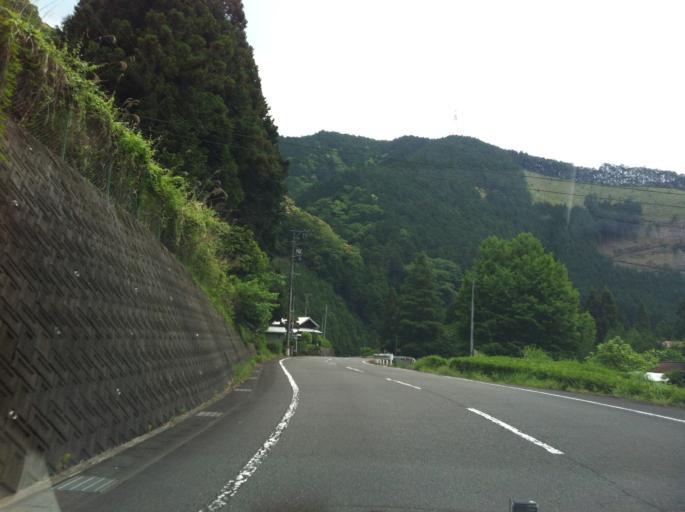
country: JP
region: Shizuoka
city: Shizuoka-shi
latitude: 35.1640
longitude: 138.3263
